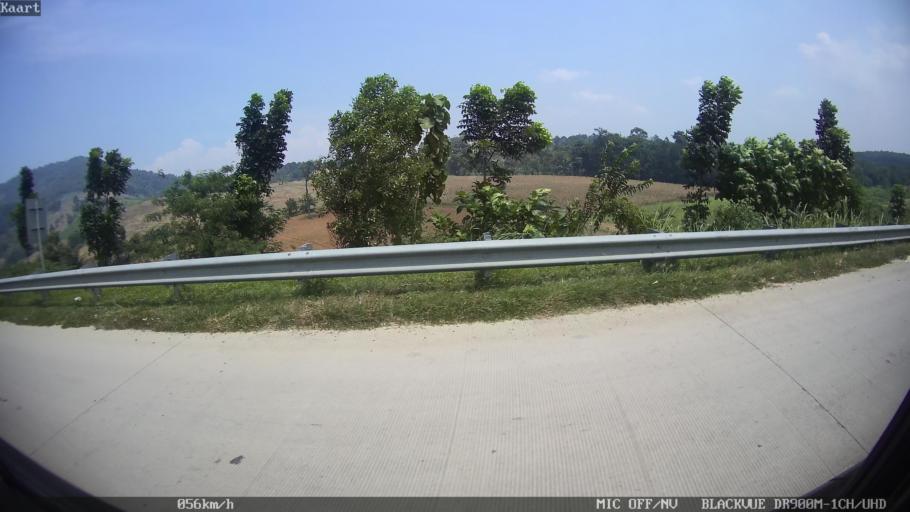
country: ID
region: Lampung
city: Panjang
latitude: -5.4002
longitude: 105.3458
